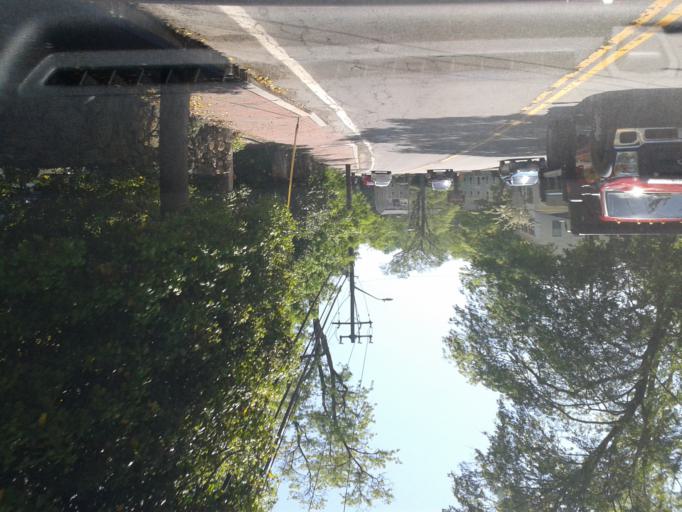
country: US
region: Rhode Island
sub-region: Washington County
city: Kingston
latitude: 41.4801
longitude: -71.5212
